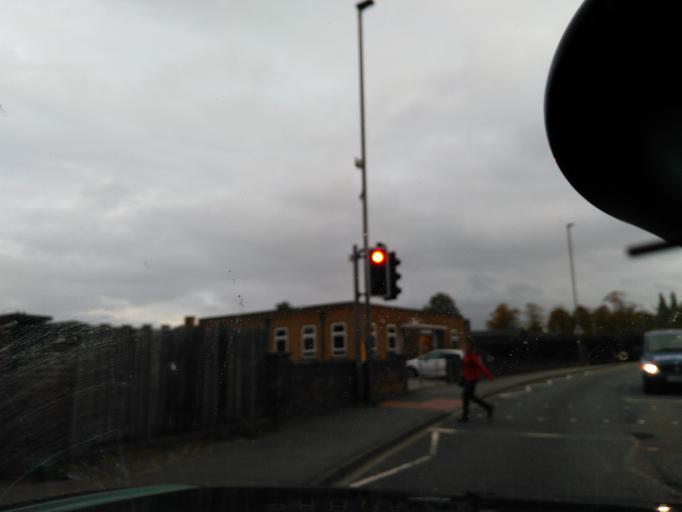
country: GB
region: England
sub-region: North Yorkshire
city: Northallerton
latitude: 54.3377
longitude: -1.4310
